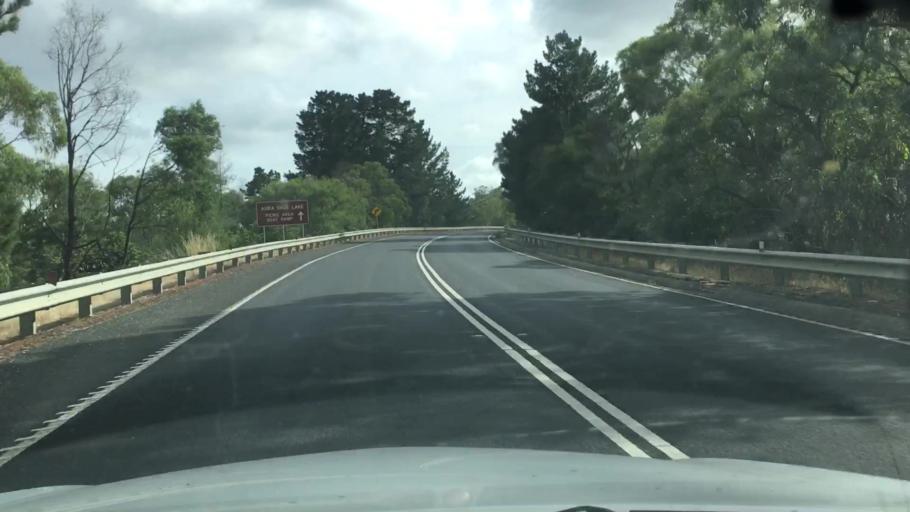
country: AU
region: Victoria
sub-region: Yarra Ranges
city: Selby
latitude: -37.9393
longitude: 145.3830
